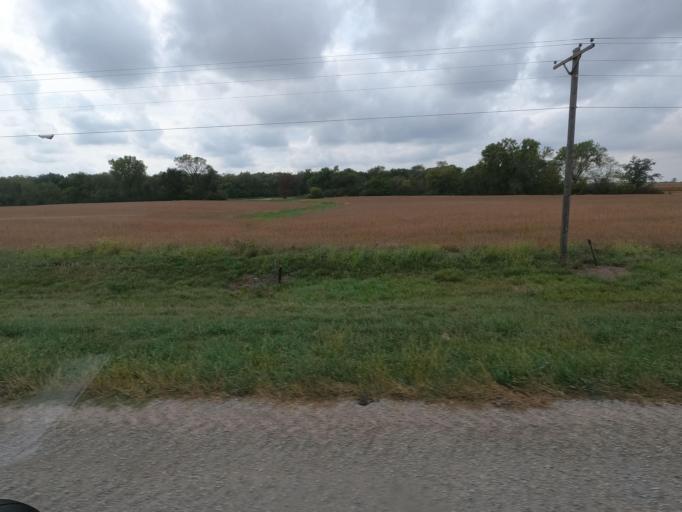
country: US
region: Iowa
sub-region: Wapello County
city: Ottumwa
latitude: 40.9781
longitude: -92.2366
